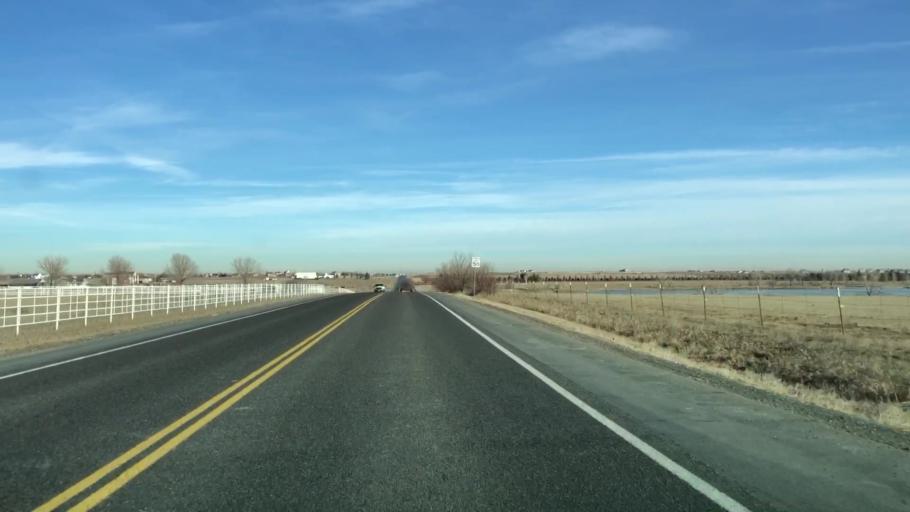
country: US
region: Colorado
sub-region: Weld County
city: Windsor
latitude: 40.4217
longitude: -104.9443
